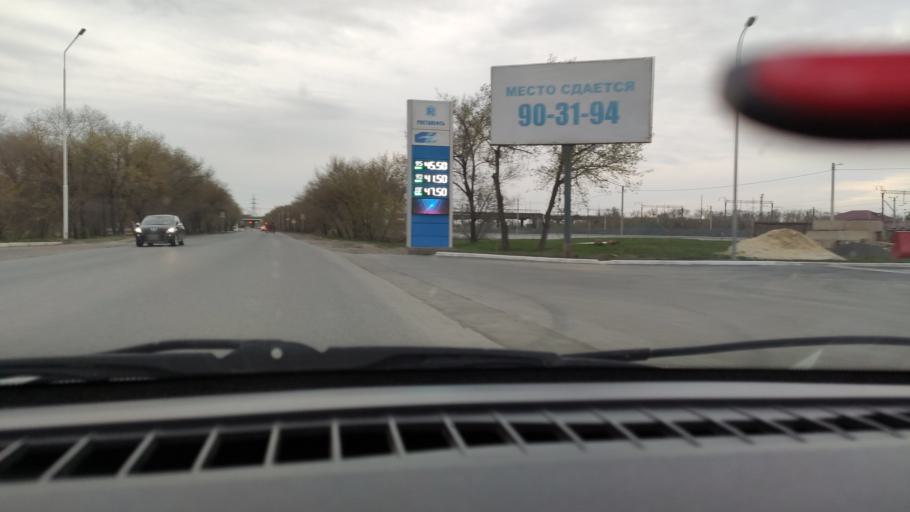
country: RU
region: Orenburg
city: Orenburg
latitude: 51.8332
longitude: 55.1117
